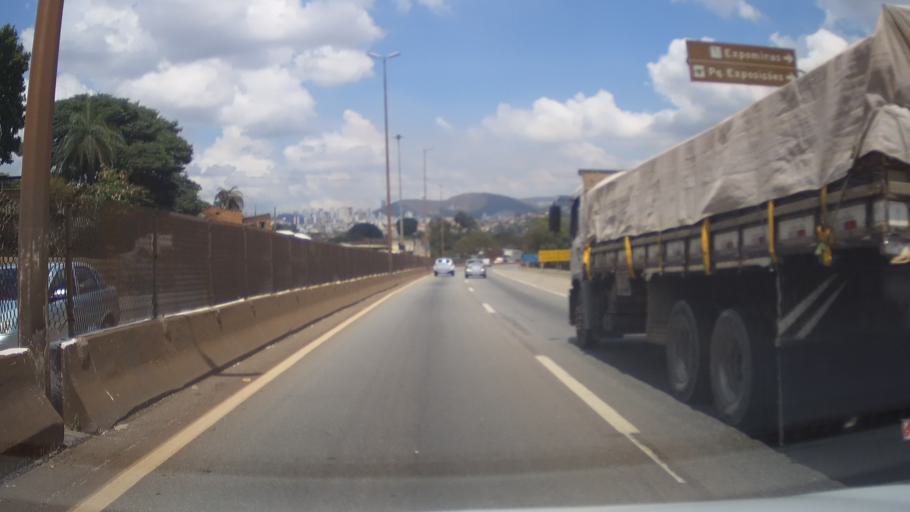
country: BR
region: Minas Gerais
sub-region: Contagem
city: Contagem
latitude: -19.9539
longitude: -44.0053
